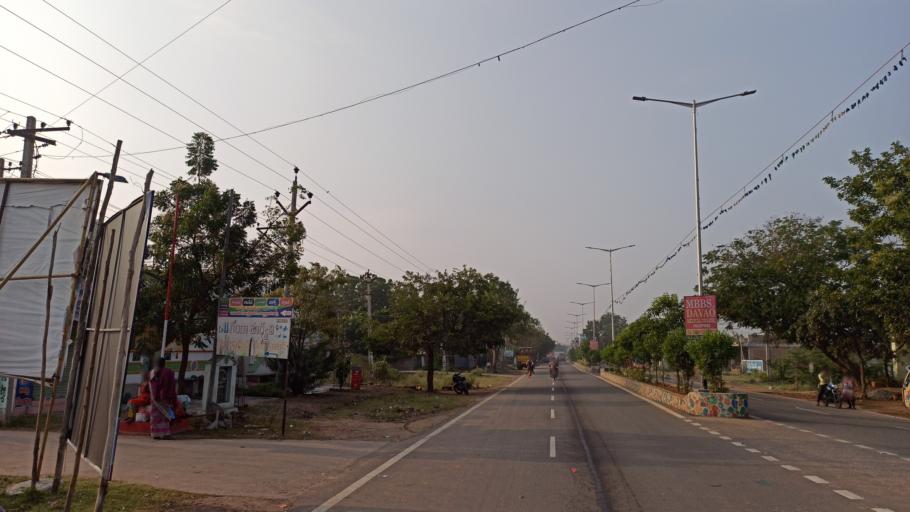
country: IN
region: Andhra Pradesh
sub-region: Guntur
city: Narasaraopet
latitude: 16.2503
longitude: 80.0572
